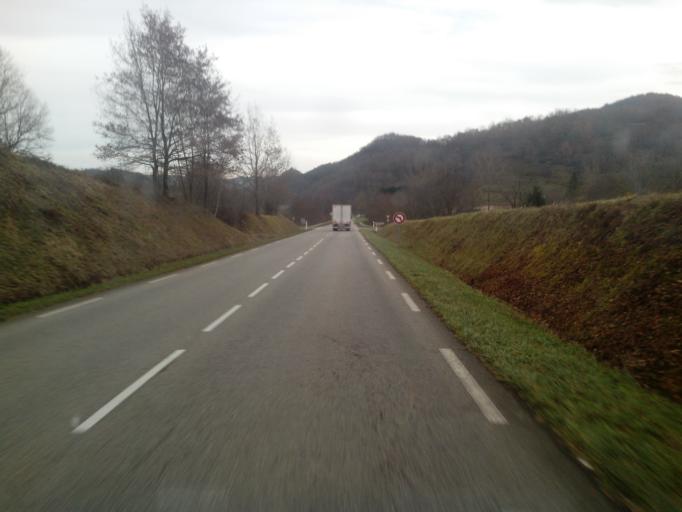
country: FR
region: Midi-Pyrenees
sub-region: Departement de l'Ariege
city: Montjoie-en-Couserans
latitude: 42.9951
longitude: 1.3198
